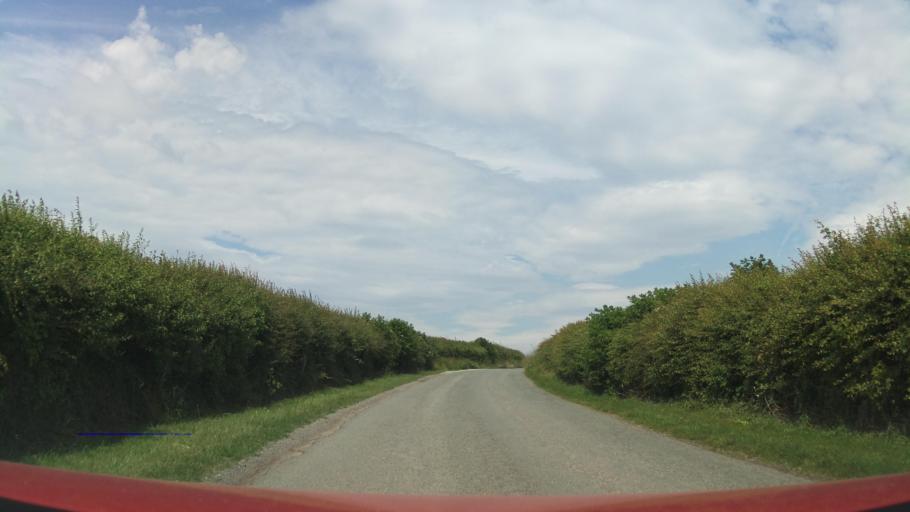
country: GB
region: Wales
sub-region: Vale of Glamorgan
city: Wick
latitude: 51.4407
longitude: -3.5689
